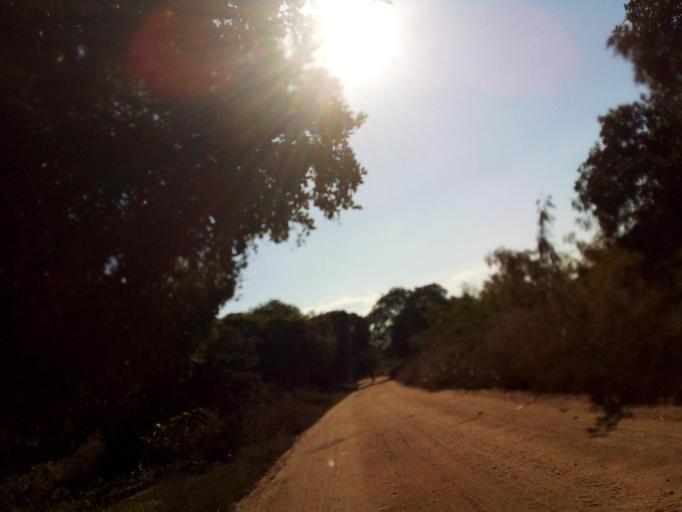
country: MZ
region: Zambezia
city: Quelimane
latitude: -17.5052
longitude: 36.5867
